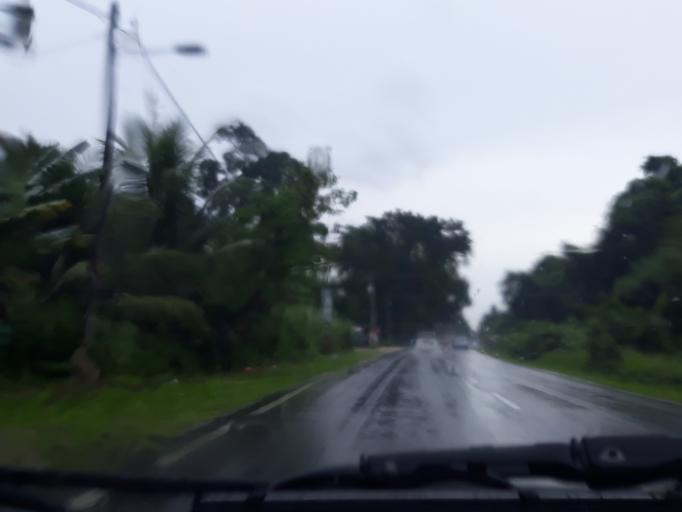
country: MY
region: Kedah
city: Kulim
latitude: 5.3554
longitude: 100.5829
